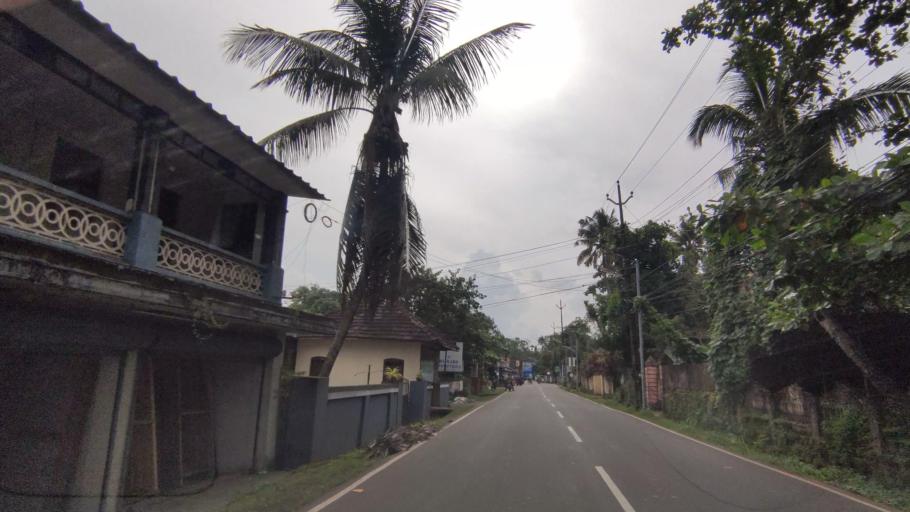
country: IN
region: Kerala
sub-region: Kottayam
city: Kottayam
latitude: 9.5846
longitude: 76.5160
